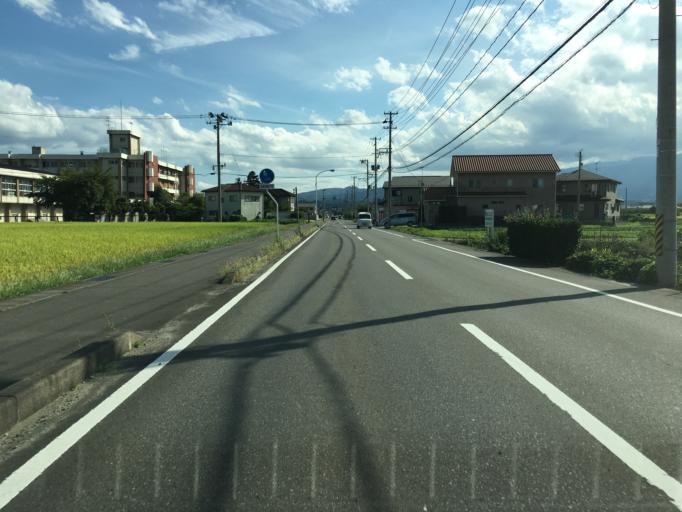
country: JP
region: Fukushima
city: Fukushima-shi
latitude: 37.7625
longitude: 140.4212
